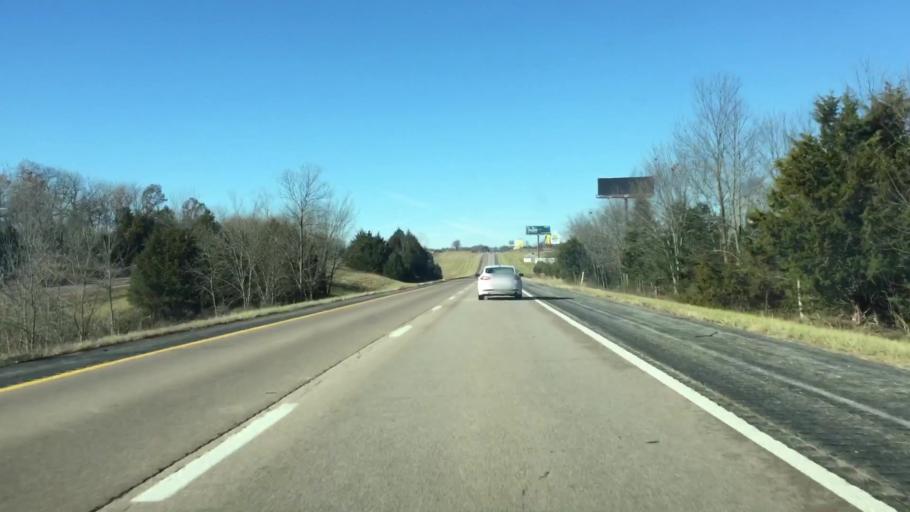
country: US
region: Missouri
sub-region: Miller County
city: Eldon
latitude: 38.3678
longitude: -92.4943
